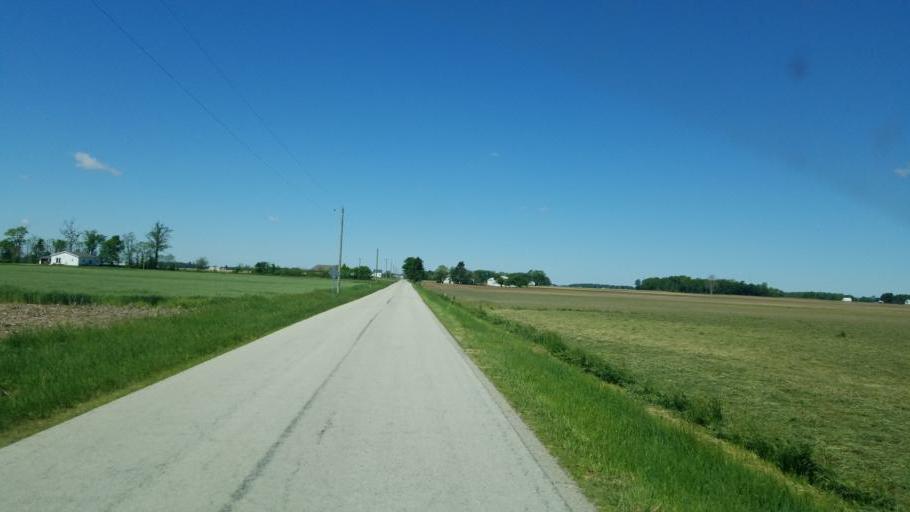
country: US
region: Ohio
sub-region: Shelby County
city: Jackson Center
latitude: 40.4175
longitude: -84.0078
